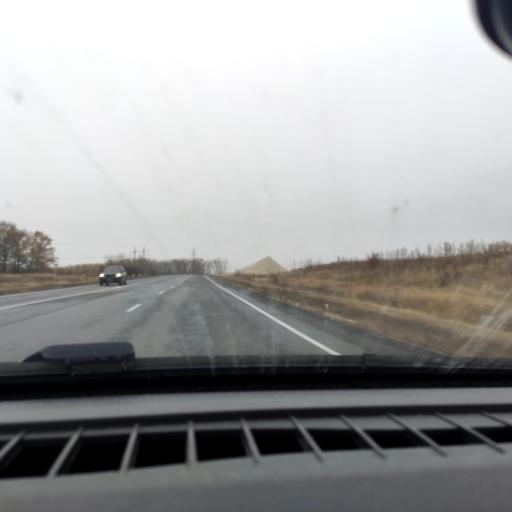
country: RU
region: Voronezj
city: Ostrogozhsk
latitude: 50.9418
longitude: 39.0555
